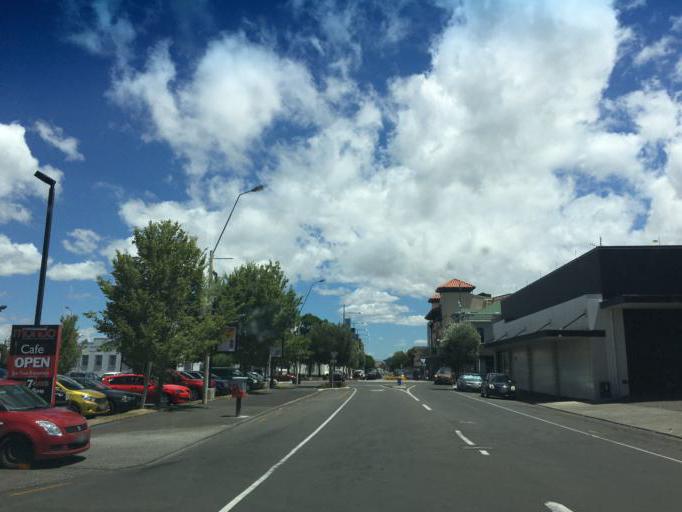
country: NZ
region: Hawke's Bay
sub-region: Hastings District
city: Hastings
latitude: -39.6443
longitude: 176.8469
